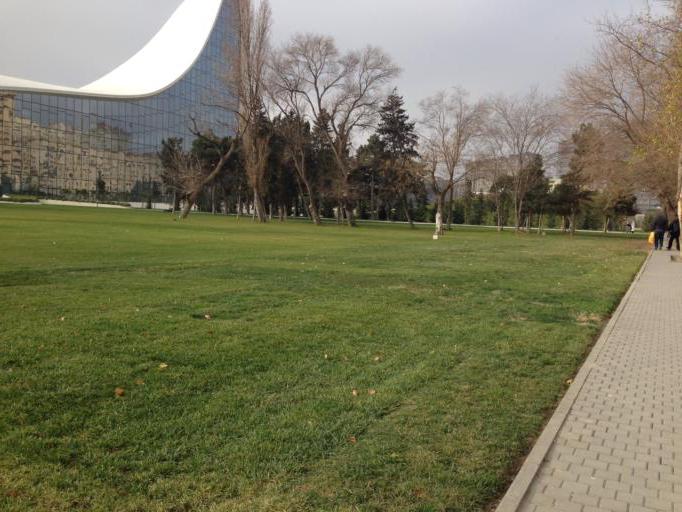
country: AZ
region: Baki
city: Baku
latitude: 40.3967
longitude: 49.8701
